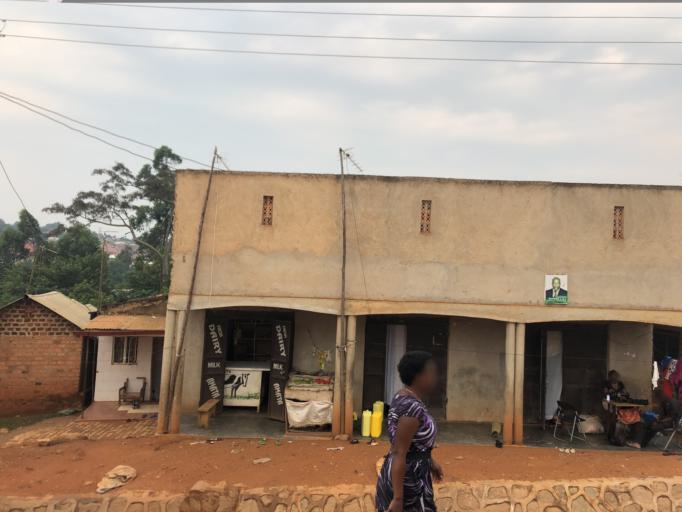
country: UG
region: Central Region
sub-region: Mukono District
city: Mukono
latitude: 0.3459
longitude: 32.7639
